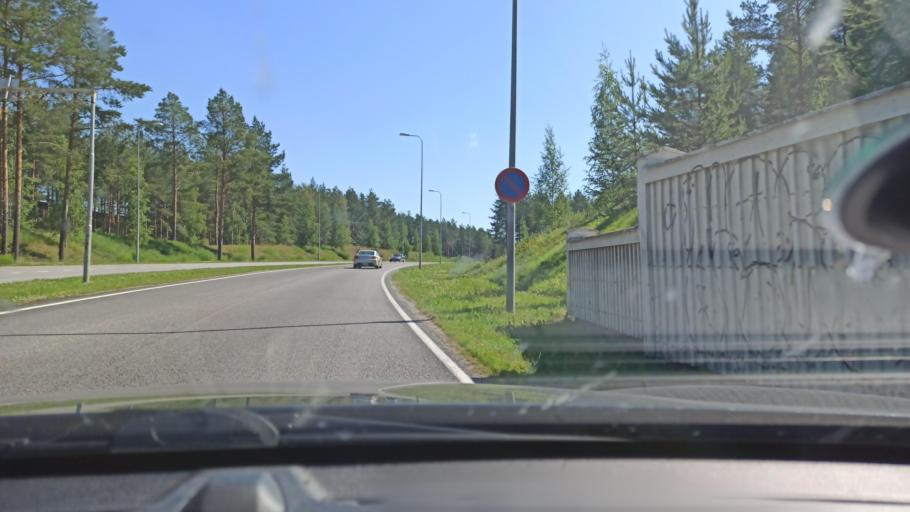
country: FI
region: Northern Ostrobothnia
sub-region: Oulu
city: Oulu
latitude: 65.0403
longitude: 25.4553
